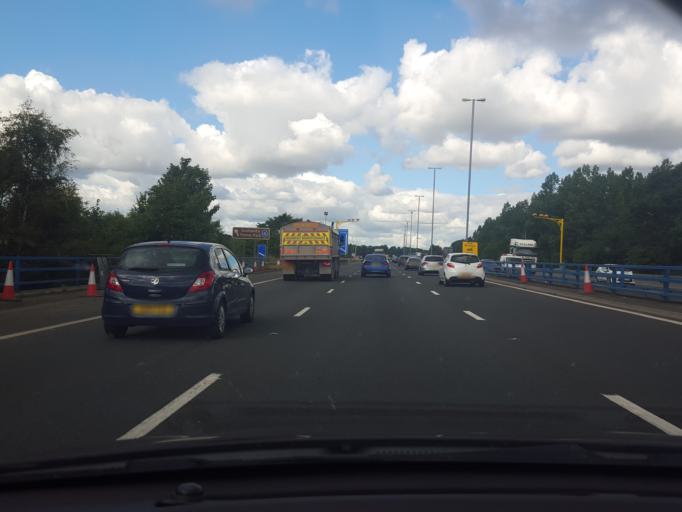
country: GB
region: Scotland
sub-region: South Lanarkshire
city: Bothwell
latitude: 55.7968
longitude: -4.0470
